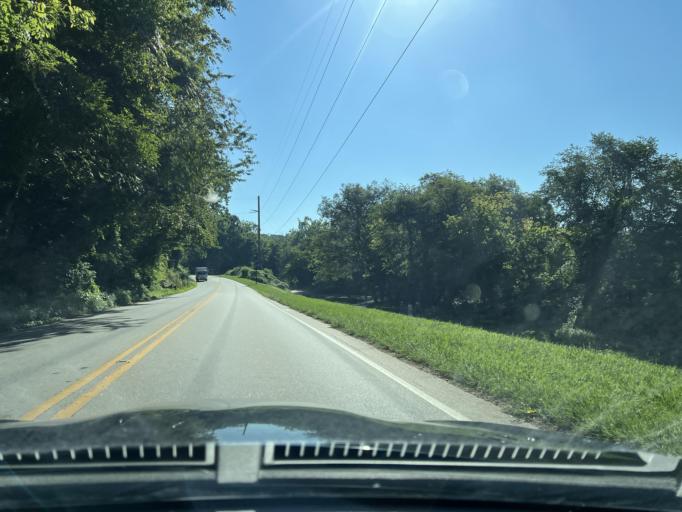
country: US
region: North Carolina
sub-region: Buncombe County
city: Asheville
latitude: 35.5680
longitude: -82.5670
